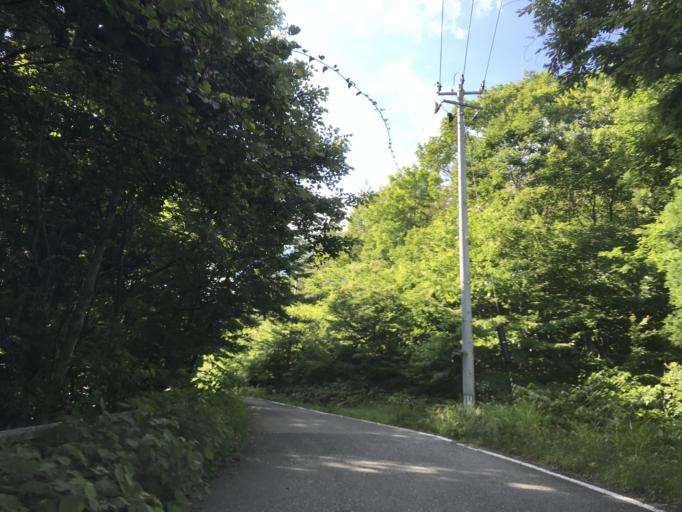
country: JP
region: Iwate
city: Ichinoseki
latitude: 38.8962
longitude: 140.8885
